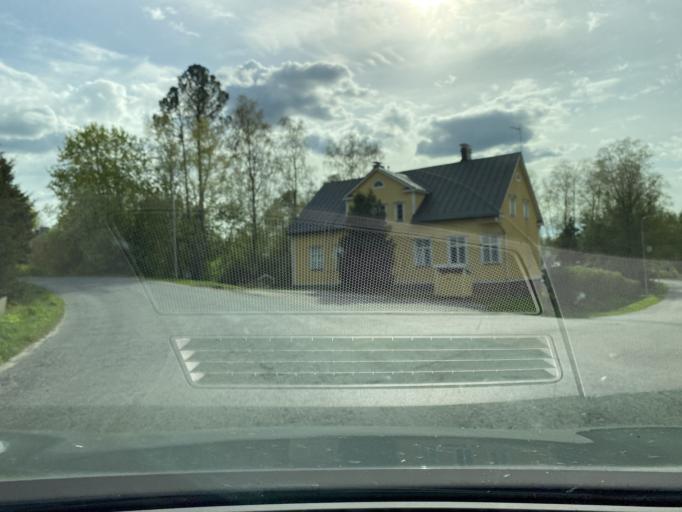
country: FI
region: Varsinais-Suomi
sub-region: Salo
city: Kiikala
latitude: 60.4594
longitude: 23.5501
